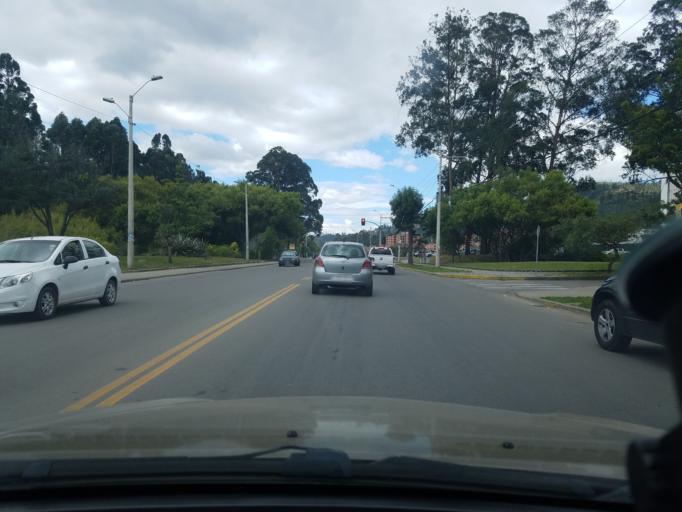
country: EC
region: Azuay
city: Cuenca
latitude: -2.8982
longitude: -78.9728
